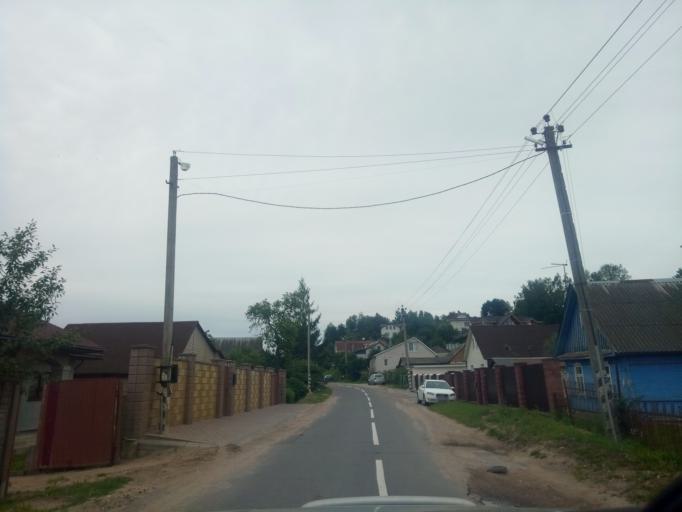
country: BY
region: Minsk
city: Zhdanovichy
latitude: 53.9285
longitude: 27.3837
